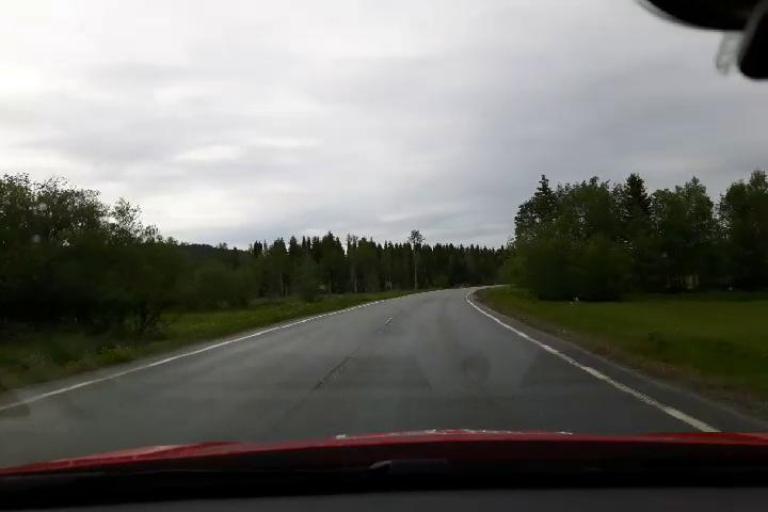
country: SE
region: Jaemtland
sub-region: Bergs Kommun
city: Hoverberg
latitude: 62.9063
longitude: 14.3334
